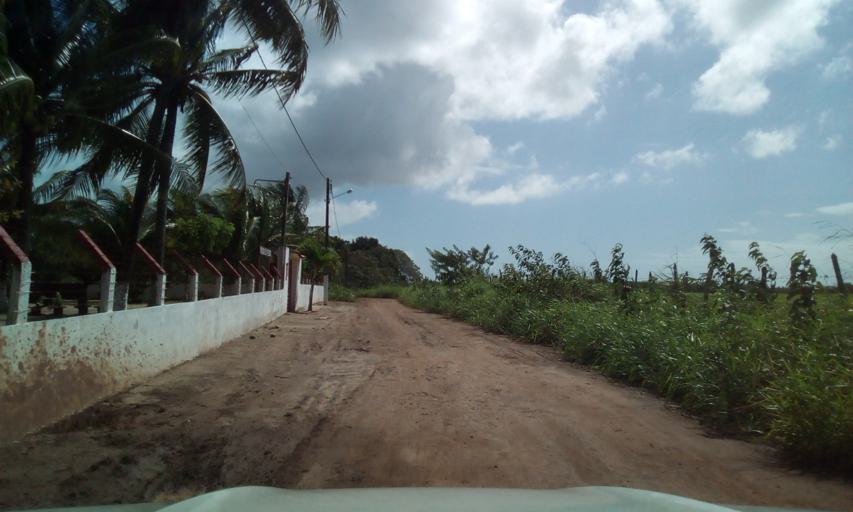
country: BR
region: Paraiba
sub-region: Conde
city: Conde
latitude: -7.2180
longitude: -34.8207
